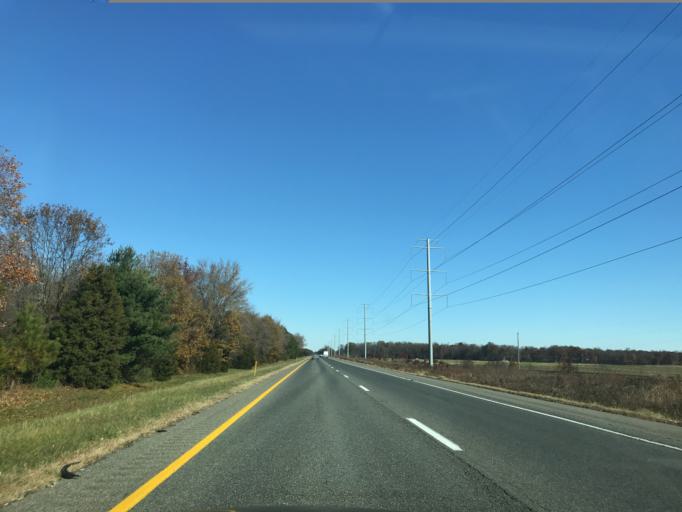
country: US
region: Maryland
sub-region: Queen Anne's County
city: Centreville
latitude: 39.0810
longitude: -75.9756
